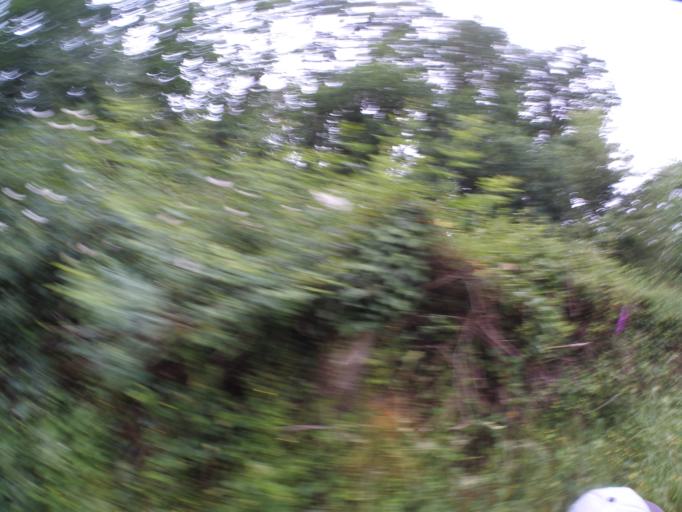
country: FR
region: Pays de la Loire
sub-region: Departement de la Vendee
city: Nesmy
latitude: 46.6049
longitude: -1.3744
